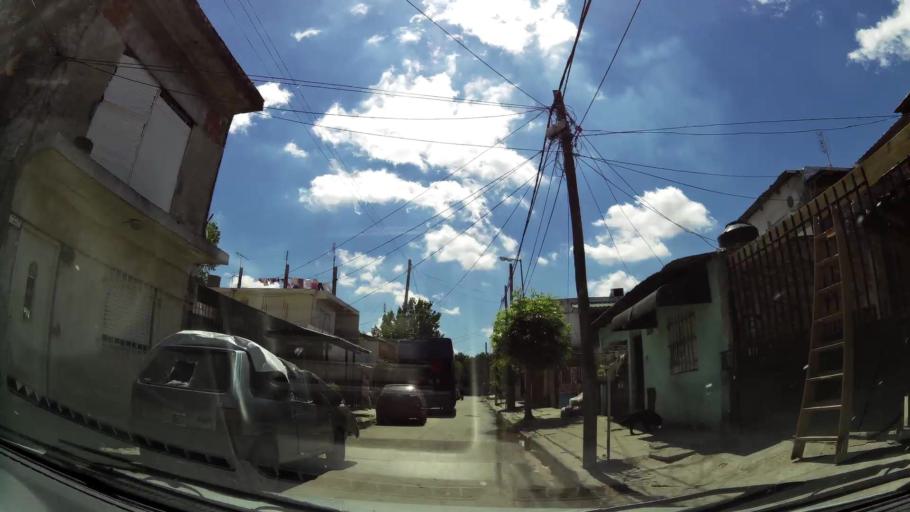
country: AR
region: Buenos Aires
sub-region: Partido de Lanus
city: Lanus
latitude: -34.6935
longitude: -58.4308
